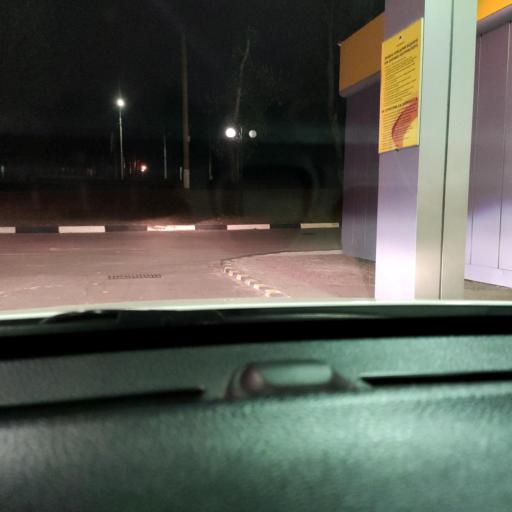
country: RU
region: Voronezj
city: Pridonskoy
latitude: 51.6482
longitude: 39.0950
